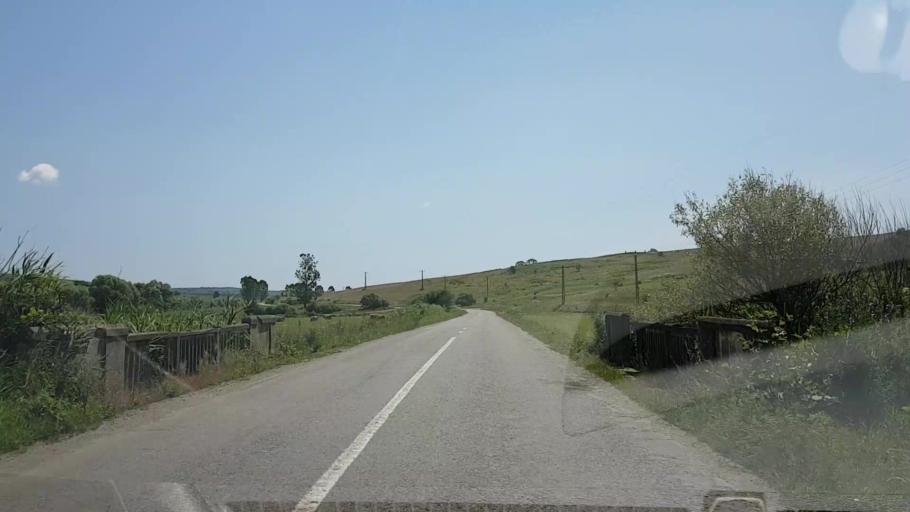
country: RO
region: Sibiu
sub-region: Comuna Merghindeal
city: Merghindeal
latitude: 45.9619
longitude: 24.7411
